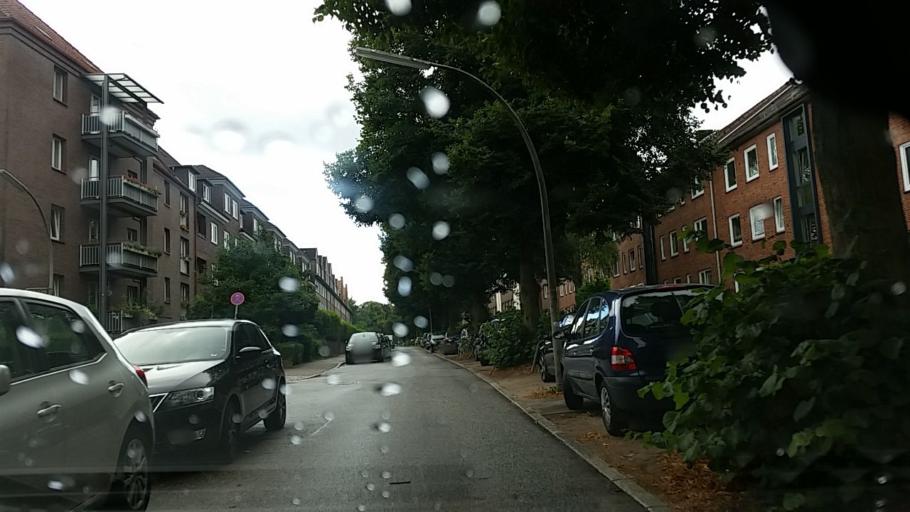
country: DE
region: Hamburg
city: Altona
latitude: 53.5536
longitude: 9.9096
